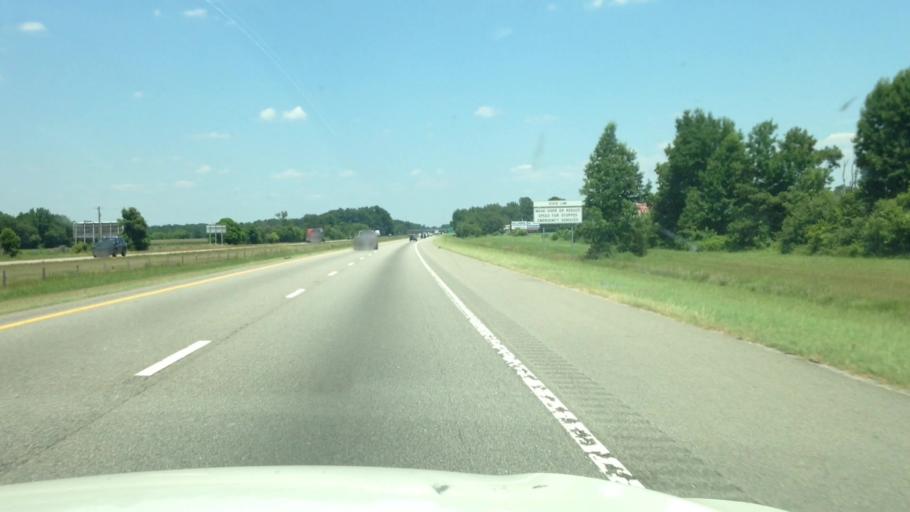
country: US
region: North Carolina
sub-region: Robeson County
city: Rowland
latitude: 34.5145
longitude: -79.2904
